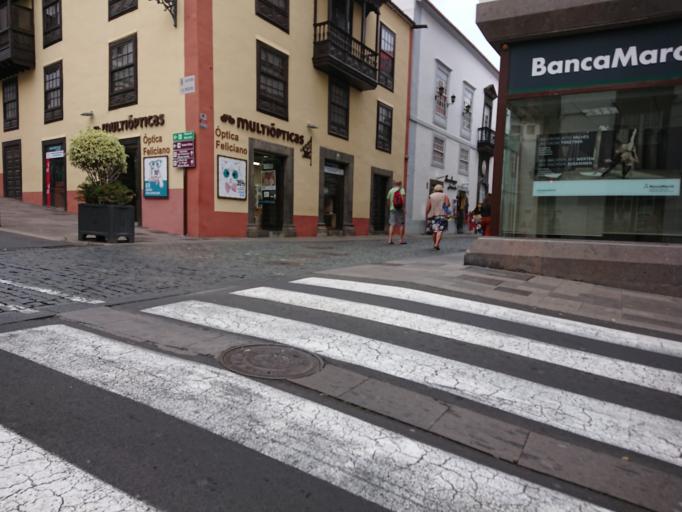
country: ES
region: Canary Islands
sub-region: Provincia de Santa Cruz de Tenerife
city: Santa Cruz de la Palma
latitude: 28.6837
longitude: -17.7643
